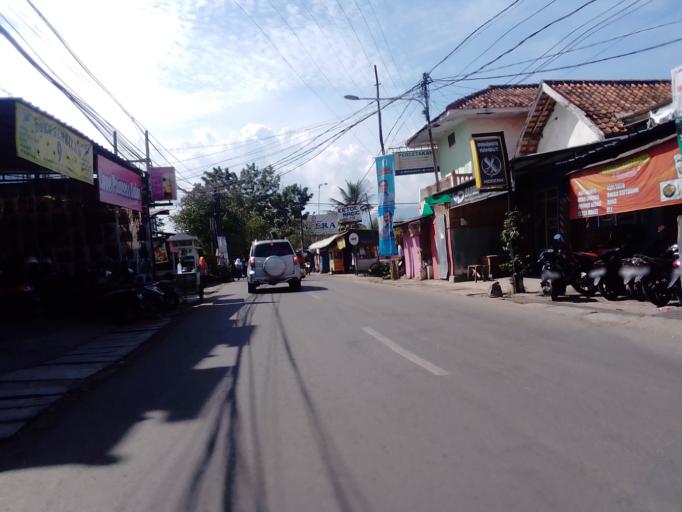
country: ID
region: West Java
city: Bandung
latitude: -6.9406
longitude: 107.6638
